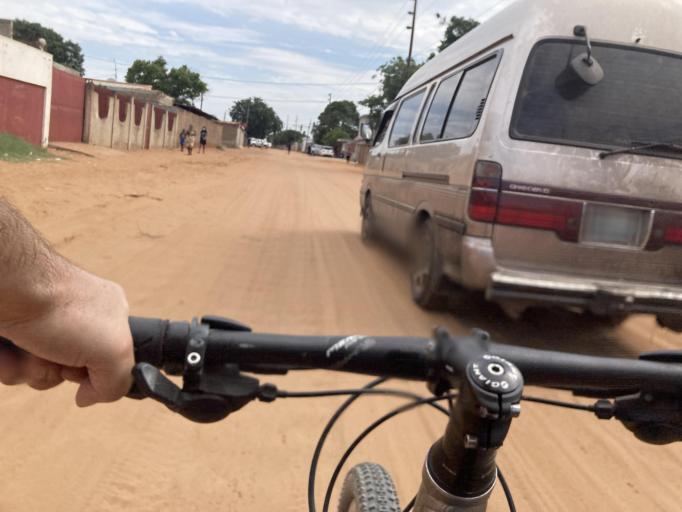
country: MZ
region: Maputo City
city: Maputo
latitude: -25.8950
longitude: 32.6073
